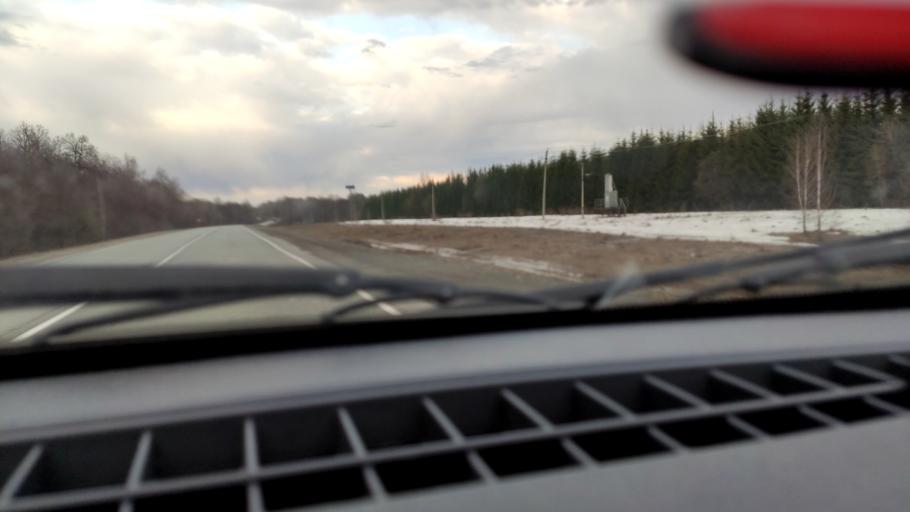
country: RU
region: Bashkortostan
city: Kudeyevskiy
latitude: 54.8065
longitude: 56.6299
